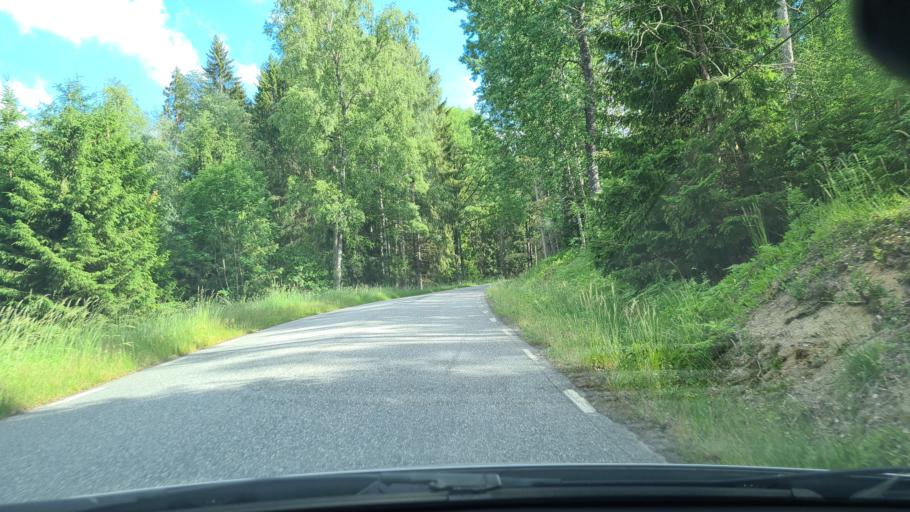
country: SE
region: Stockholm
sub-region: Varmdo Kommun
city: Mortnas
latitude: 59.4018
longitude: 18.4622
